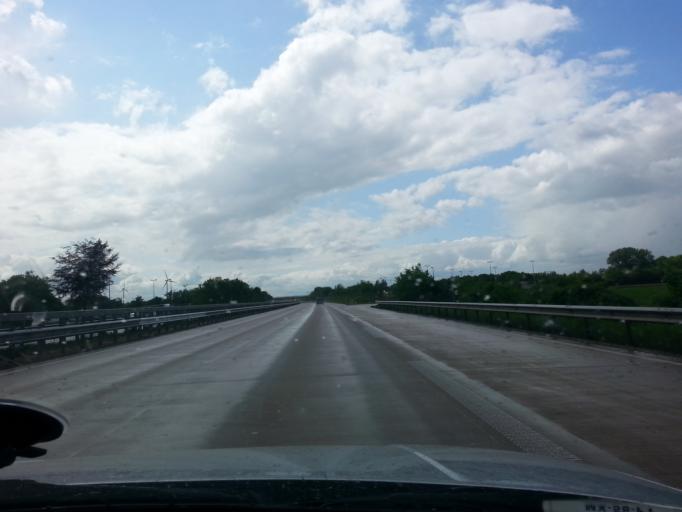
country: DE
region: Lower Saxony
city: Isterberg
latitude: 52.3363
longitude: 7.1106
